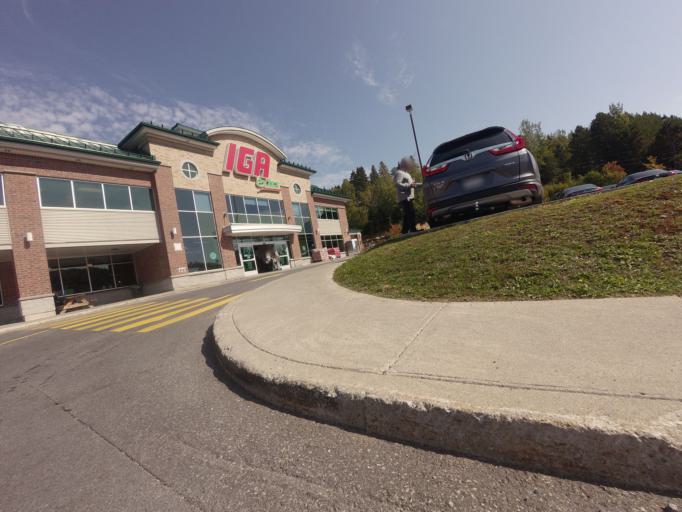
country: CA
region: Quebec
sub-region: Laurentides
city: Sainte-Agathe-des-Monts
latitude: 46.0467
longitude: -74.2780
